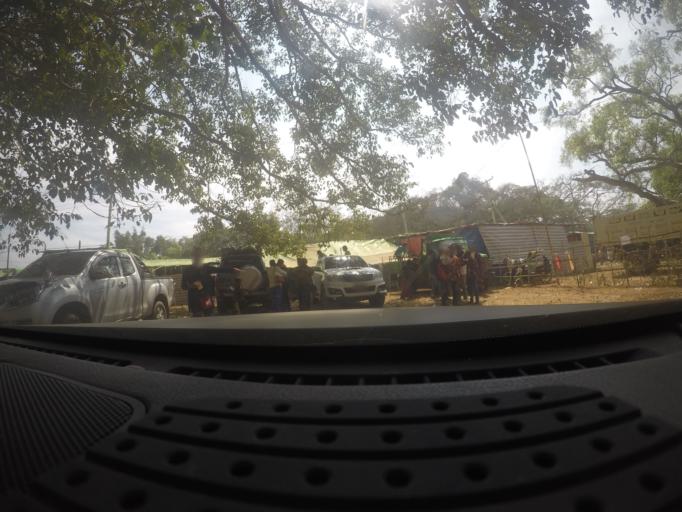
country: MM
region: Shan
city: Taunggyi
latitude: 20.9307
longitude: 96.6581
